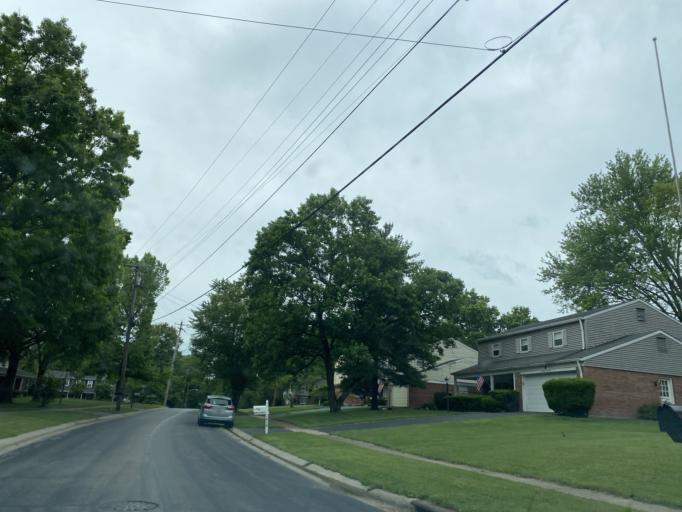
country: US
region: Ohio
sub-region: Hamilton County
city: Salem Heights
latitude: 39.0852
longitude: -84.4030
